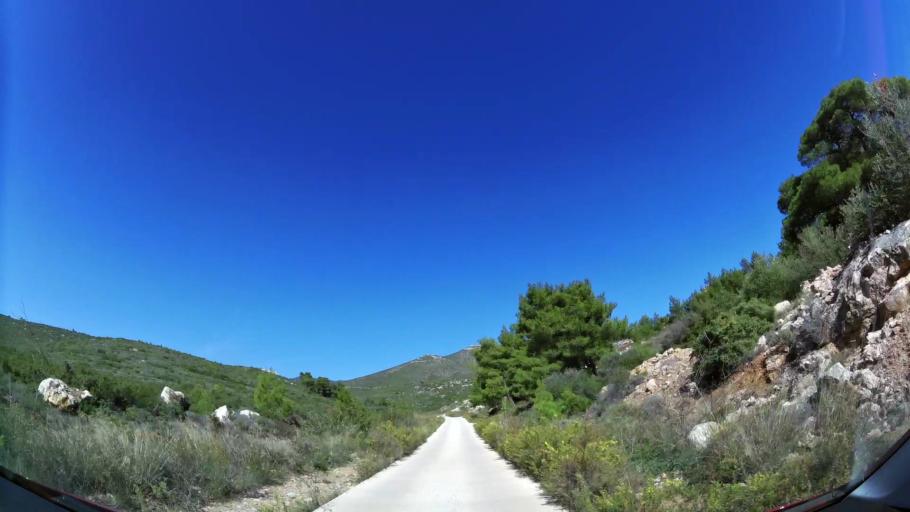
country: GR
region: Attica
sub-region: Nomarchia Anatolikis Attikis
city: Dioni
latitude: 38.0303
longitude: 23.9211
